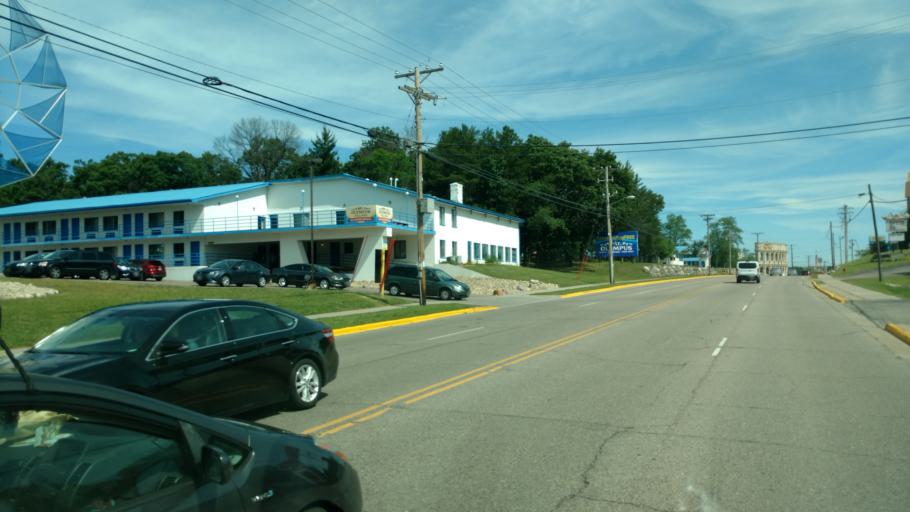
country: US
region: Wisconsin
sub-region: Sauk County
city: Lake Delton
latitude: 43.6076
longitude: -89.7914
